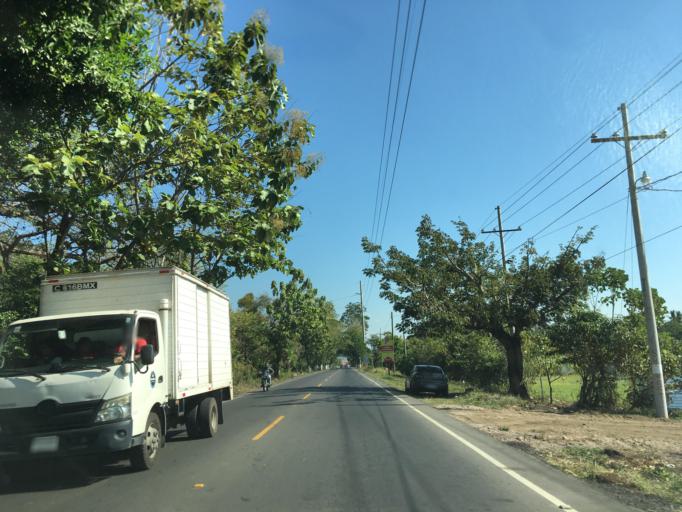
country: GT
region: Escuintla
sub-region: Municipio de La Democracia
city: La Democracia
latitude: 14.2200
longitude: -90.9521
